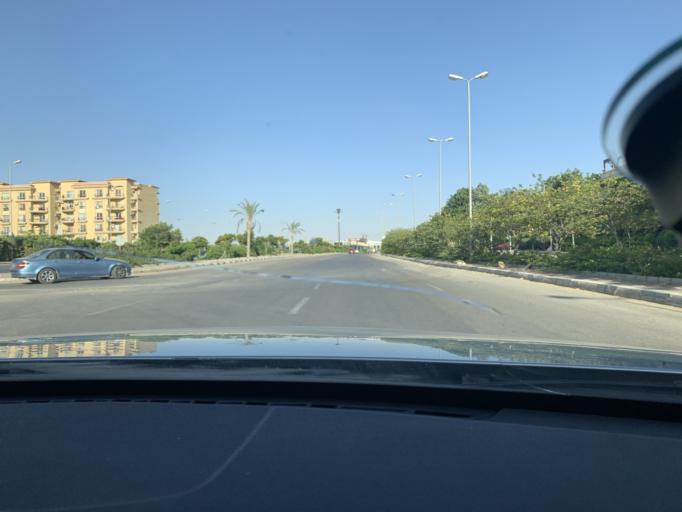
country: EG
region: Muhafazat al Qalyubiyah
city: Al Khankah
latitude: 30.0522
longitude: 31.5071
